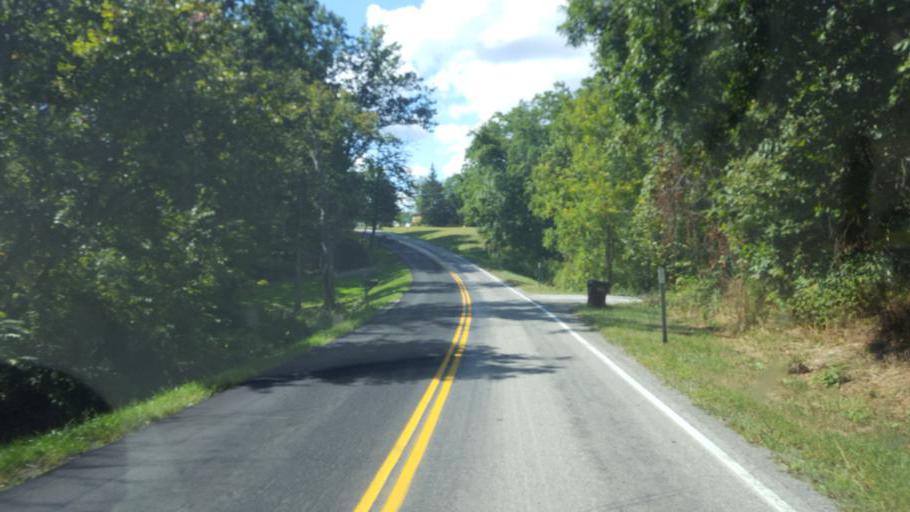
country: US
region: Ohio
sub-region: Lorain County
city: Lagrange
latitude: 41.1884
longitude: -82.1078
